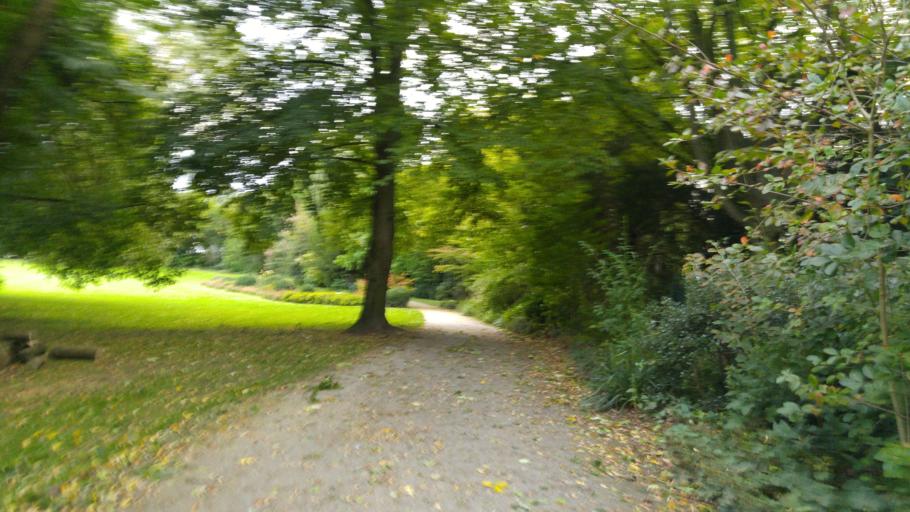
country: DE
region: North Rhine-Westphalia
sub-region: Regierungsbezirk Detmold
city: Bielefeld
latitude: 52.0386
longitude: 8.5275
